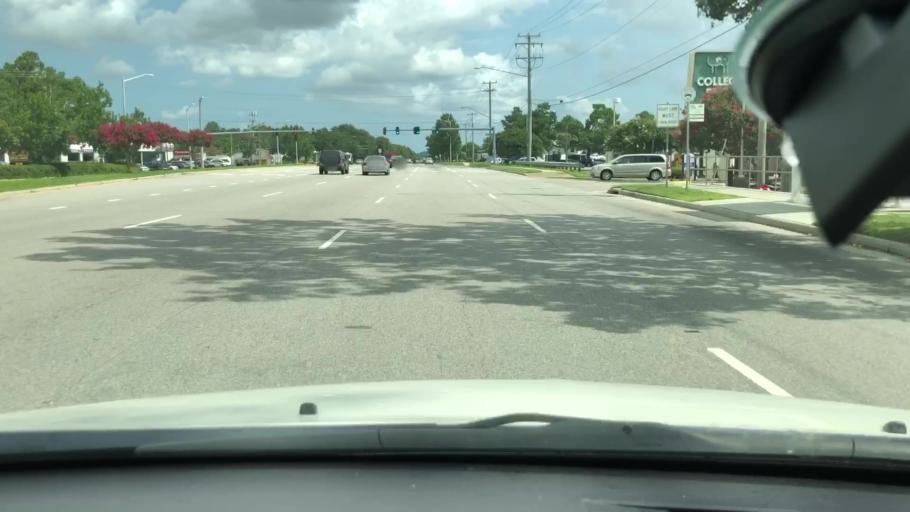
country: US
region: Virginia
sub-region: City of Chesapeake
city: Chesapeake
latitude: 36.8099
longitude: -76.2186
